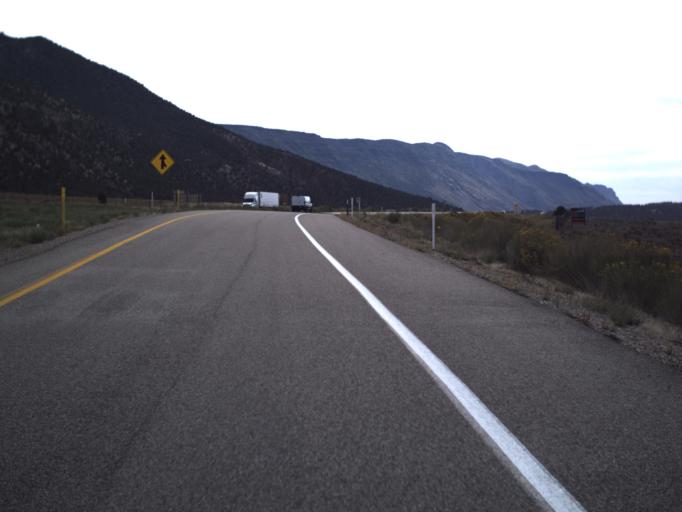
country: US
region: Utah
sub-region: Washington County
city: Toquerville
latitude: 37.4529
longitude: -113.2292
